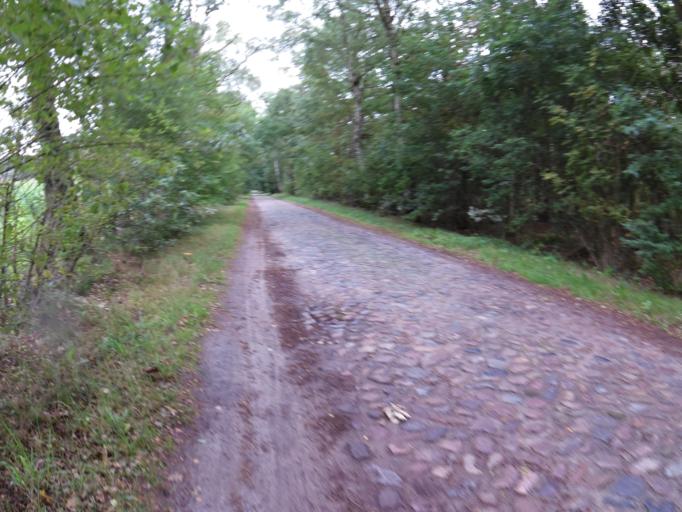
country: DE
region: Lower Saxony
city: Rotenburg
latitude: 53.1389
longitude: 9.4356
